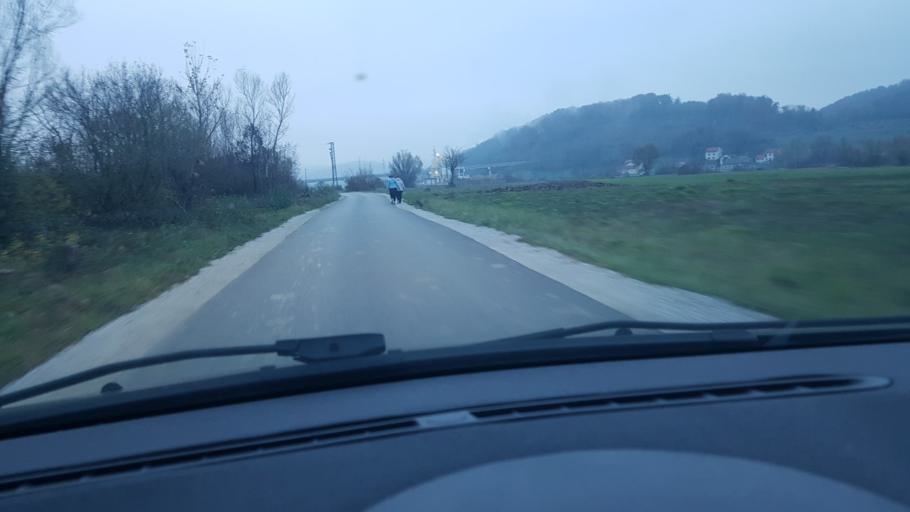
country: HR
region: Krapinsko-Zagorska
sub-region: Grad Krapina
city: Krapina
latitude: 46.1390
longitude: 15.8768
